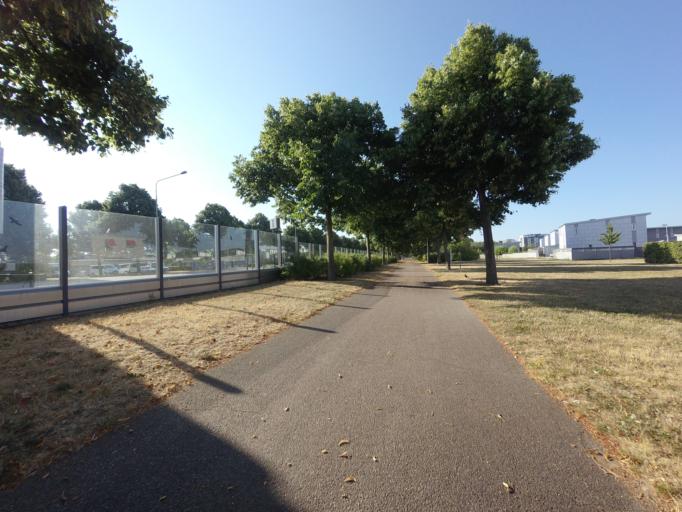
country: SE
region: Skane
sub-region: Landskrona
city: Landskrona
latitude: 55.8959
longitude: 12.8267
